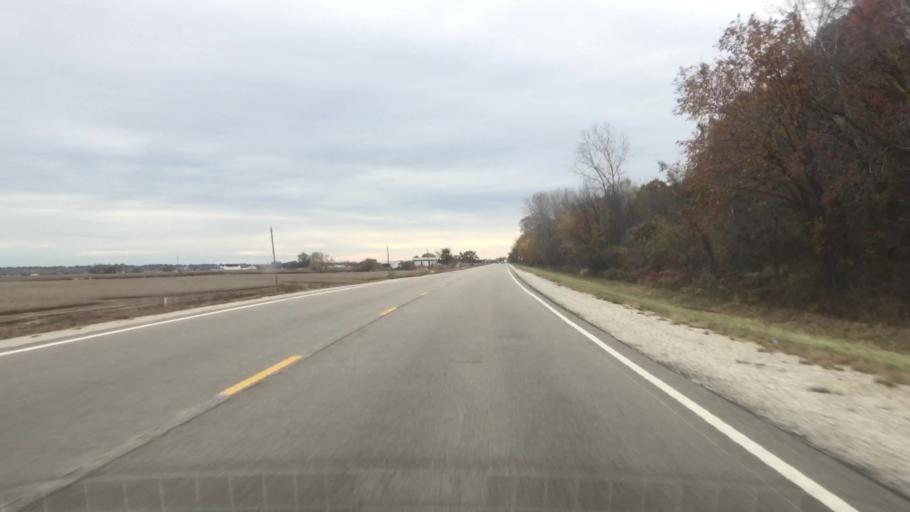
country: US
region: Missouri
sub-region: Cole County
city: Jefferson City
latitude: 38.5877
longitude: -92.1251
